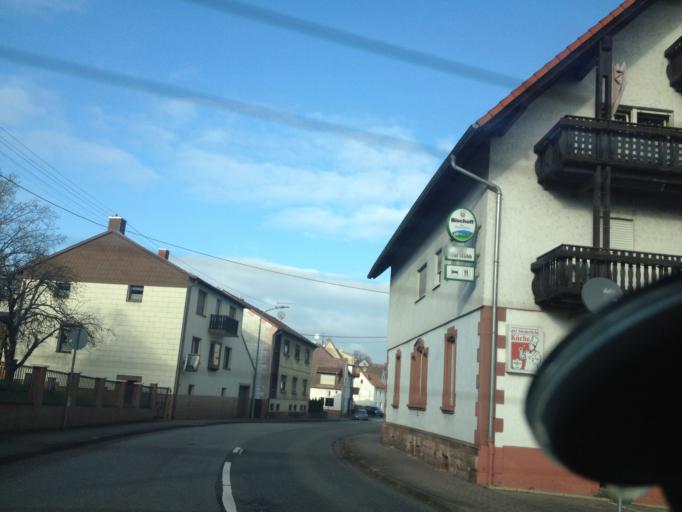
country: DE
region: Rheinland-Pfalz
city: Glan-Munchweiler
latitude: 49.4695
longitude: 7.4434
